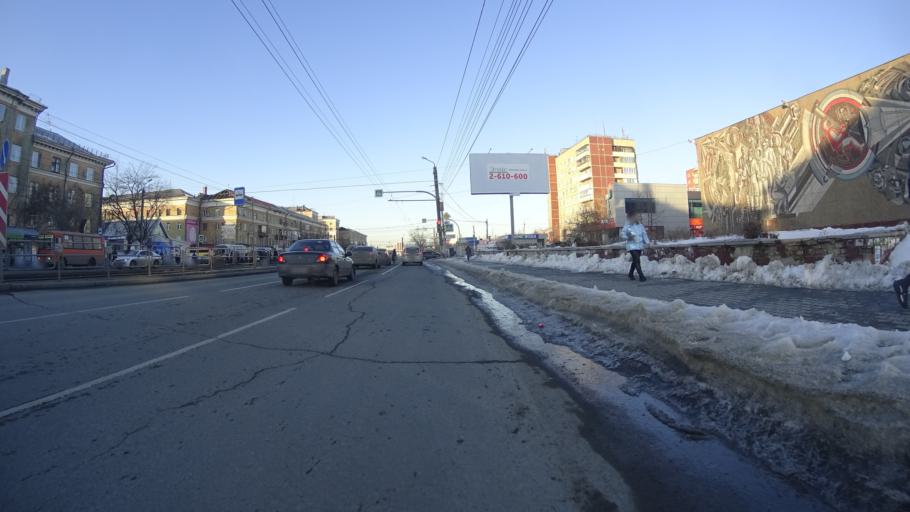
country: RU
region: Chelyabinsk
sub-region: Gorod Chelyabinsk
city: Chelyabinsk
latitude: 55.1434
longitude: 61.4438
